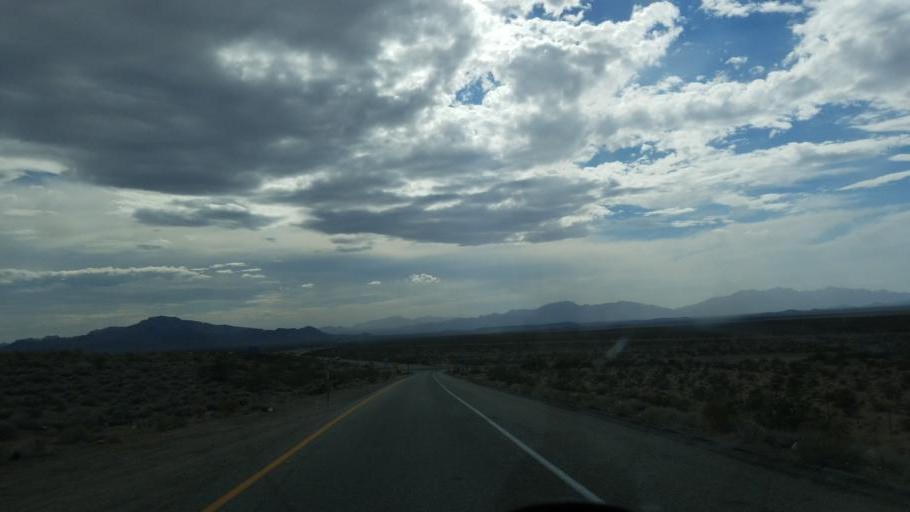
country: US
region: California
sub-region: San Bernardino County
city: Needles
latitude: 34.8132
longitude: -115.1878
